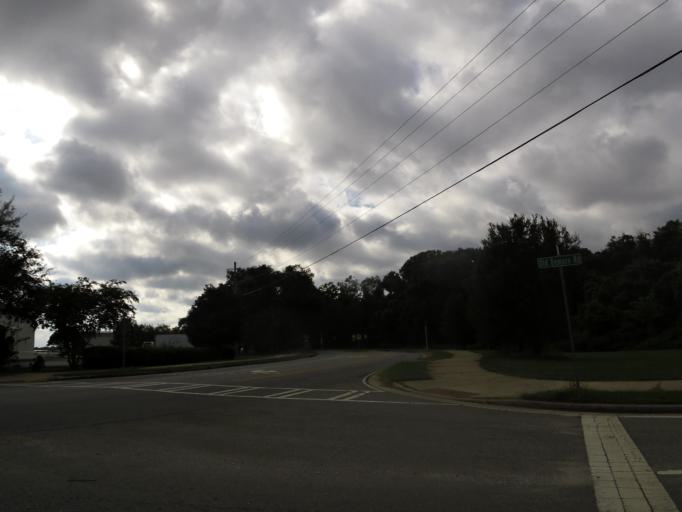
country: US
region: Georgia
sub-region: Glynn County
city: Saint Simons Island
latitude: 31.1515
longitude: -81.3808
